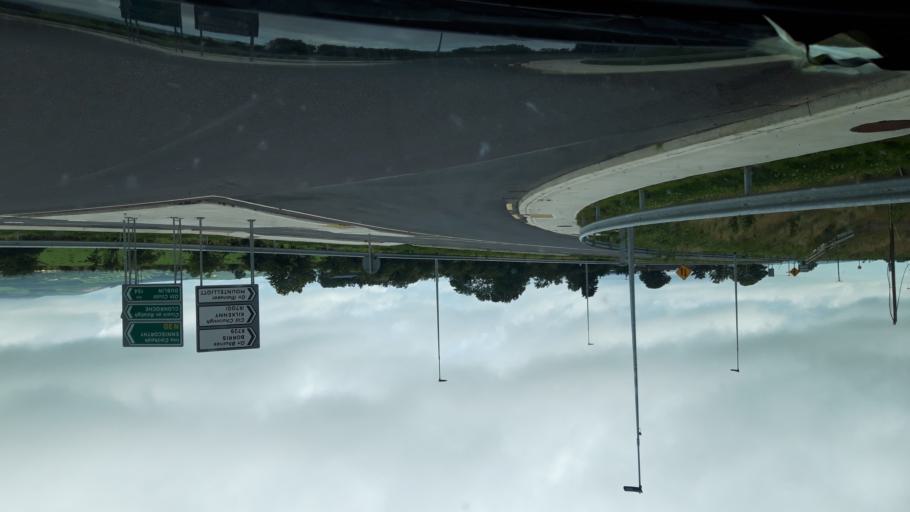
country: IE
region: Leinster
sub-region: Loch Garman
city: New Ross
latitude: 52.4183
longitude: -6.8609
